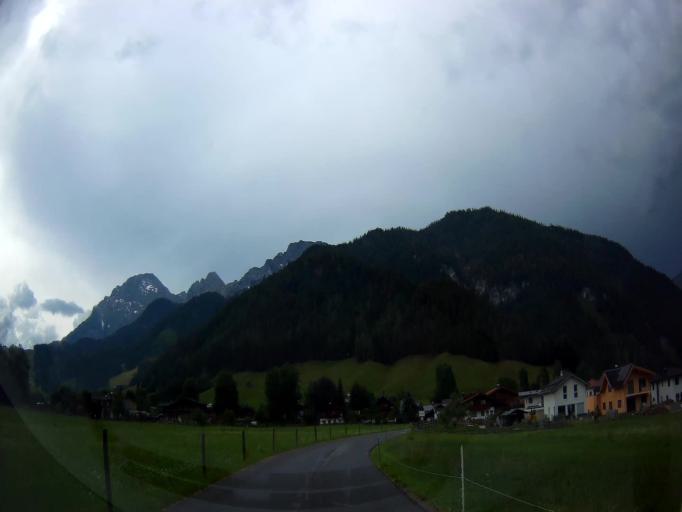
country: AT
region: Salzburg
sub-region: Politischer Bezirk Zell am See
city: Saalfelden am Steinernen Meer
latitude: 47.4488
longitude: 12.8099
